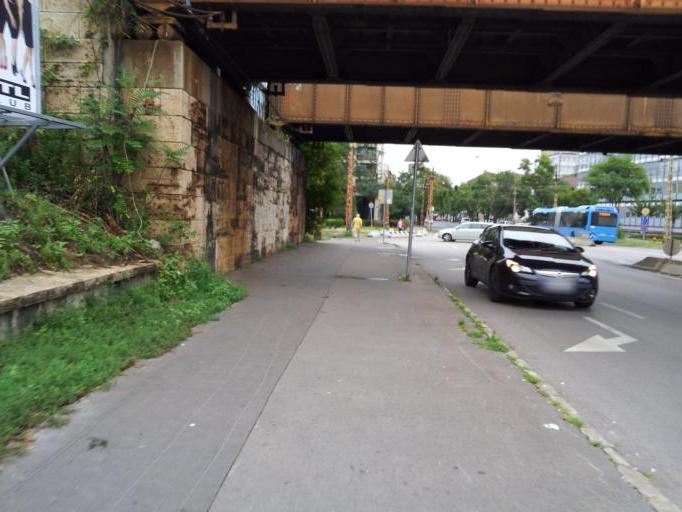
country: HU
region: Budapest
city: Budapest XIV. keruelet
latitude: 47.5120
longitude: 19.0997
